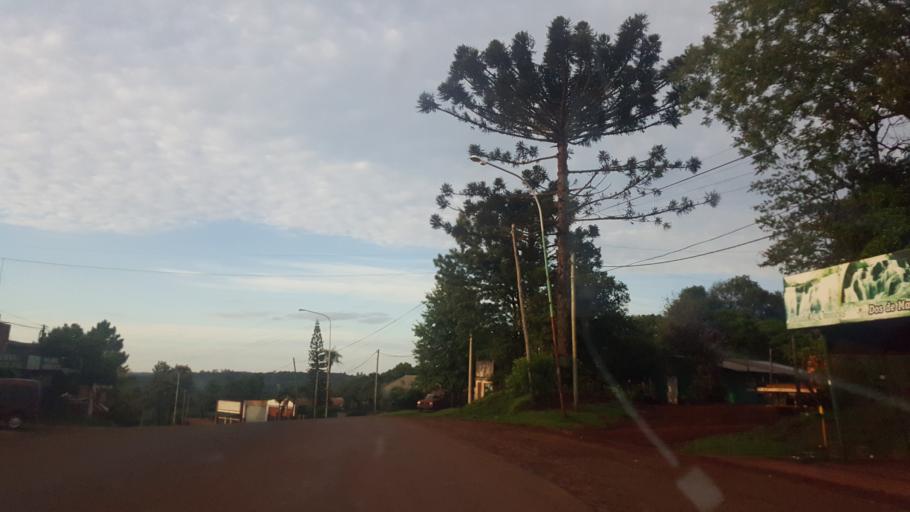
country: AR
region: Misiones
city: Dos de Mayo
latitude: -27.0264
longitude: -54.6876
